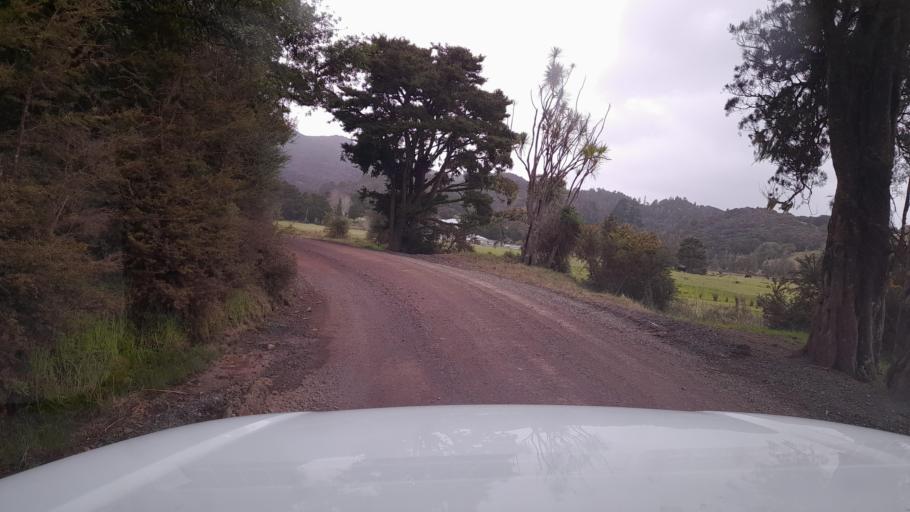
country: NZ
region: Northland
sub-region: Far North District
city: Paihia
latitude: -35.3370
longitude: 174.2317
